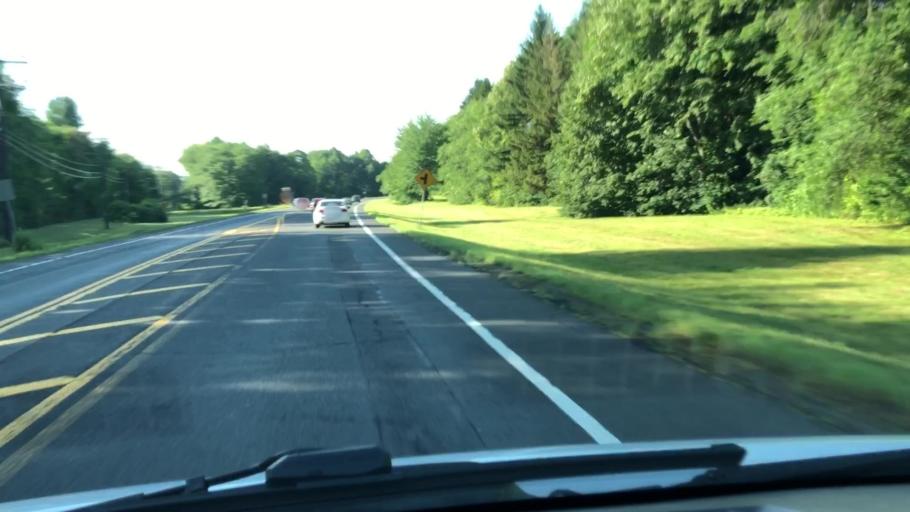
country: US
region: Massachusetts
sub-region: Hampshire County
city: North Amherst
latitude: 42.4230
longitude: -72.5386
